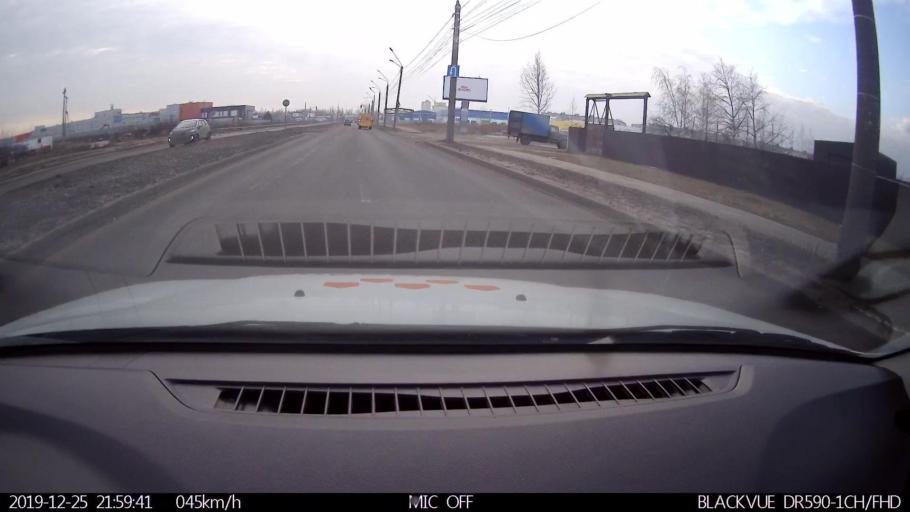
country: RU
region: Nizjnij Novgorod
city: Neklyudovo
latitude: 56.3435
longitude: 43.8889
